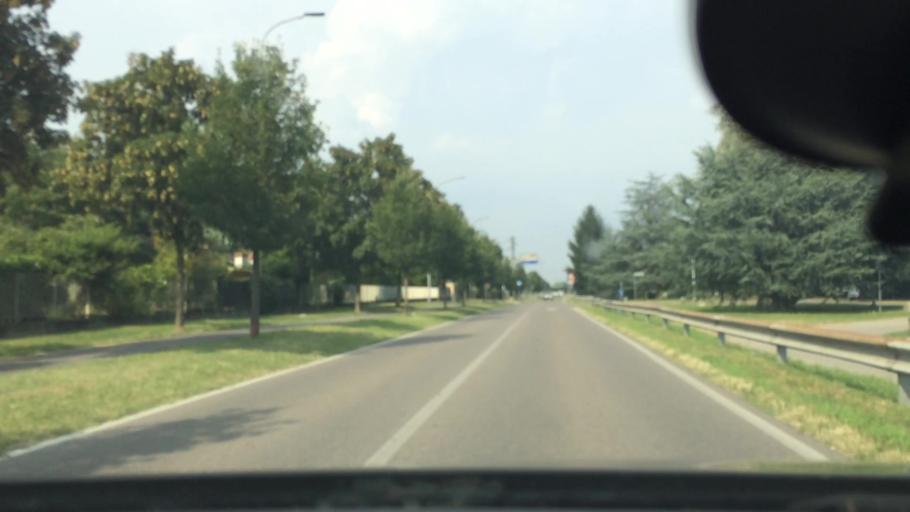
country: IT
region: Lombardy
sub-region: Citta metropolitana di Milano
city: Busto Garolfo
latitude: 45.5527
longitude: 8.8938
